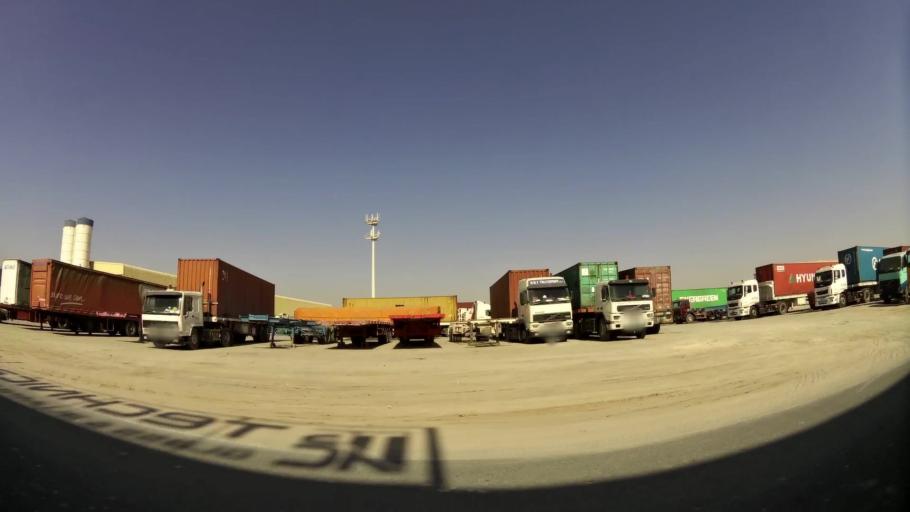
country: AE
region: Dubai
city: Dubai
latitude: 24.9908
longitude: 55.1028
